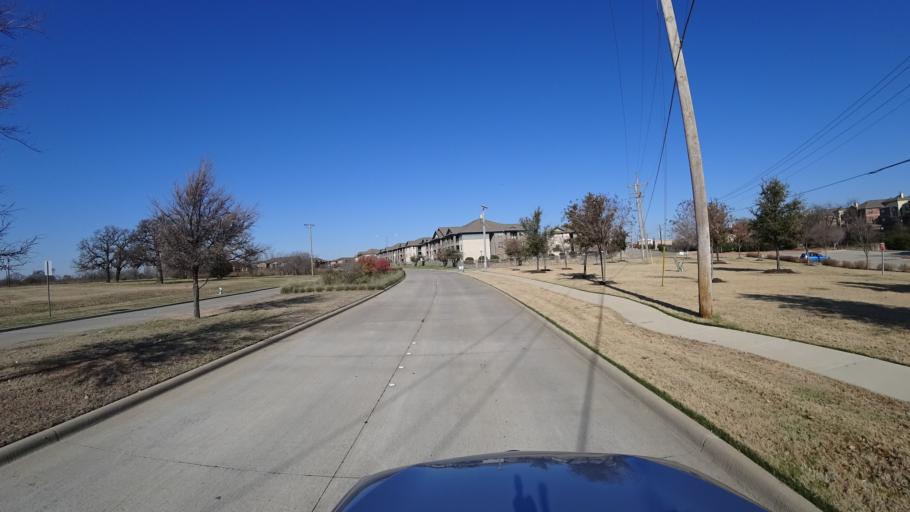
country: US
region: Texas
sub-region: Dallas County
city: Coppell
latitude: 33.0011
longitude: -97.0160
